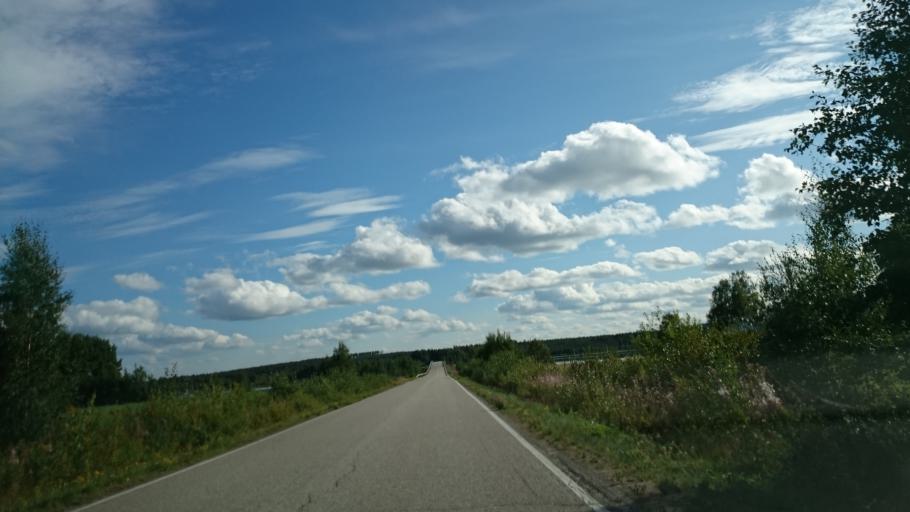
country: FI
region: Kainuu
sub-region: Kehys-Kainuu
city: Suomussalmi
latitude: 64.7457
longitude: 29.4409
